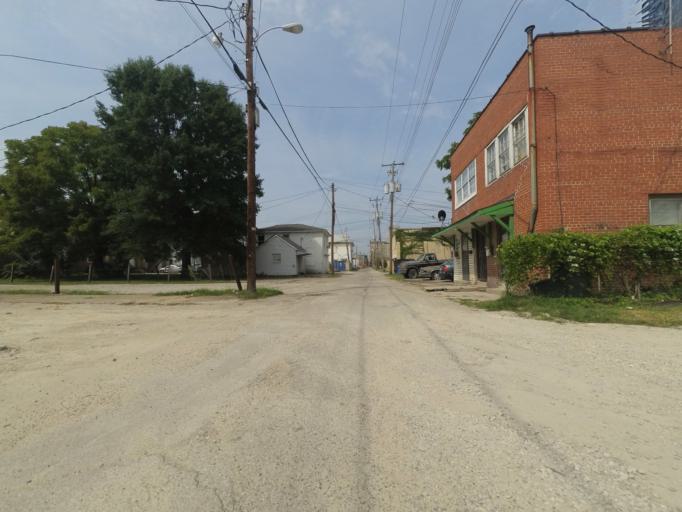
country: US
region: West Virginia
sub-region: Cabell County
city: Huntington
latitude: 38.4215
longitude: -82.4357
